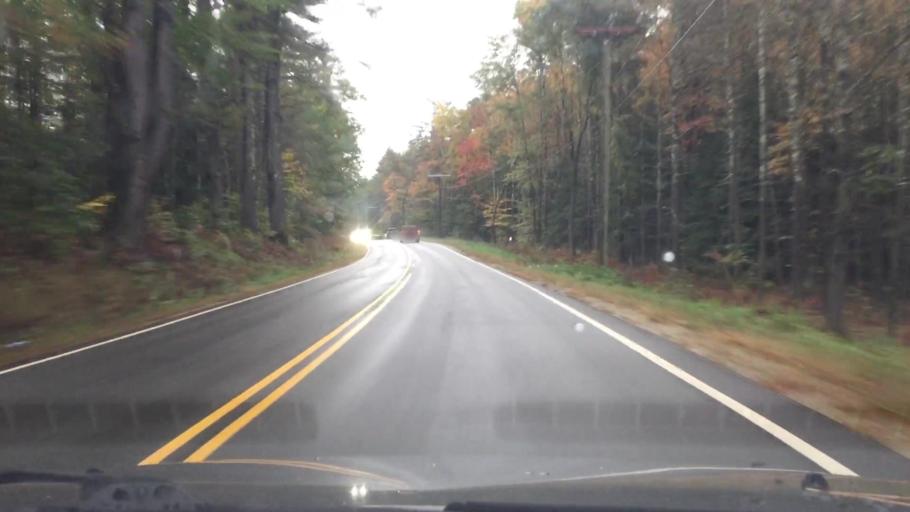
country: US
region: New Hampshire
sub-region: Cheshire County
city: Swanzey
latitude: 42.8400
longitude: -72.2791
